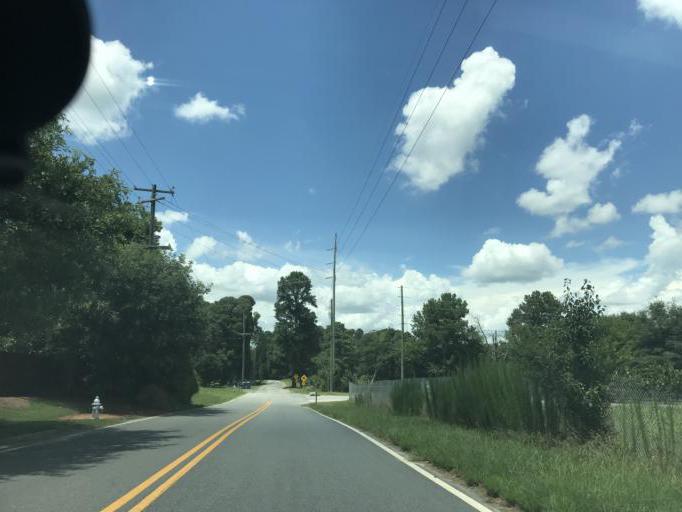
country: US
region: Georgia
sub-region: Gwinnett County
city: Suwanee
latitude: 34.0571
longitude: -84.1181
